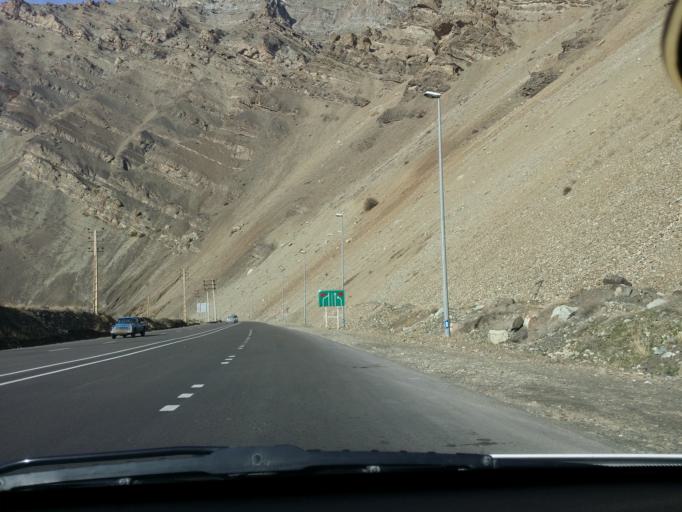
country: IR
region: Alborz
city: Karaj
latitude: 36.0127
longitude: 51.1287
